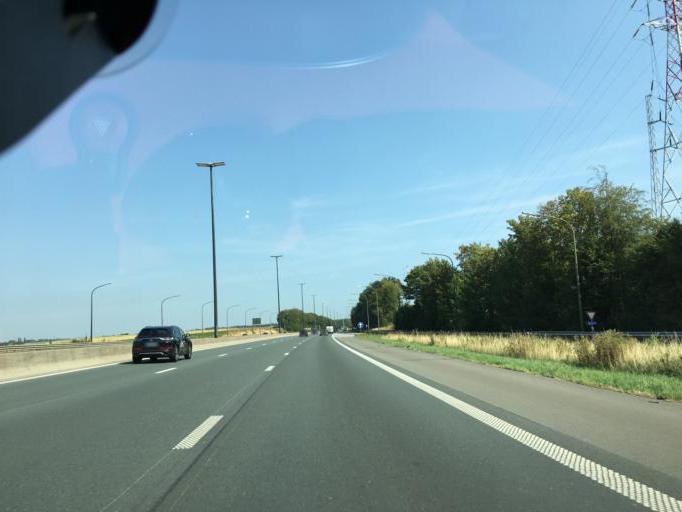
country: BE
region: Wallonia
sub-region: Province du Hainaut
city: Brunehault
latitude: 50.4816
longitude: 4.4508
